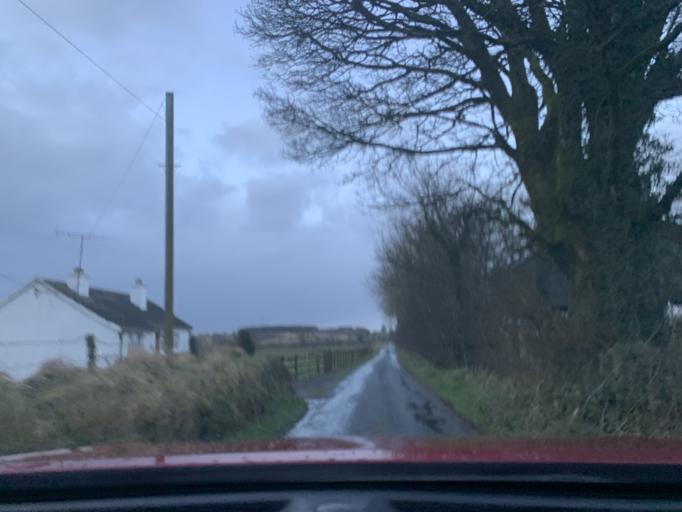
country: IE
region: Connaught
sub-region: Roscommon
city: Ballaghaderreen
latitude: 53.9673
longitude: -8.5595
